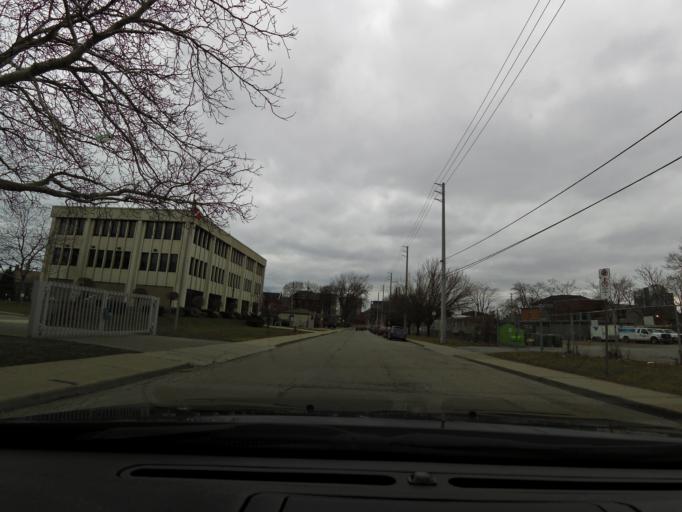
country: CA
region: Ontario
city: Hamilton
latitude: 43.2631
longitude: -79.8712
